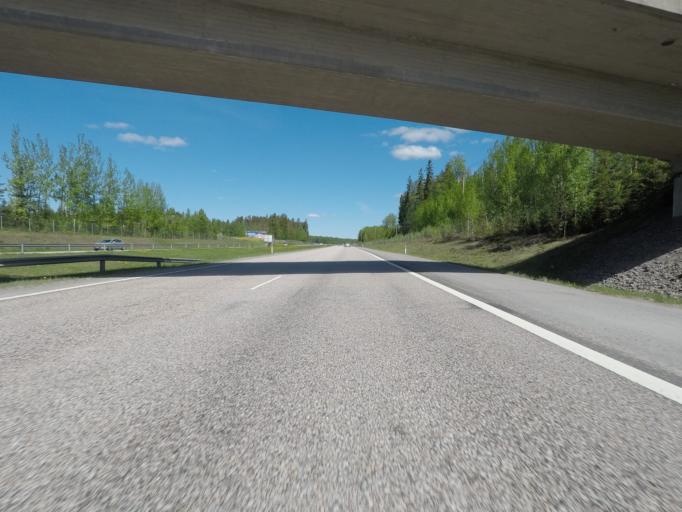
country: FI
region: Uusimaa
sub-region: Helsinki
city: Nurmijaervi
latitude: 60.4720
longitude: 24.8502
